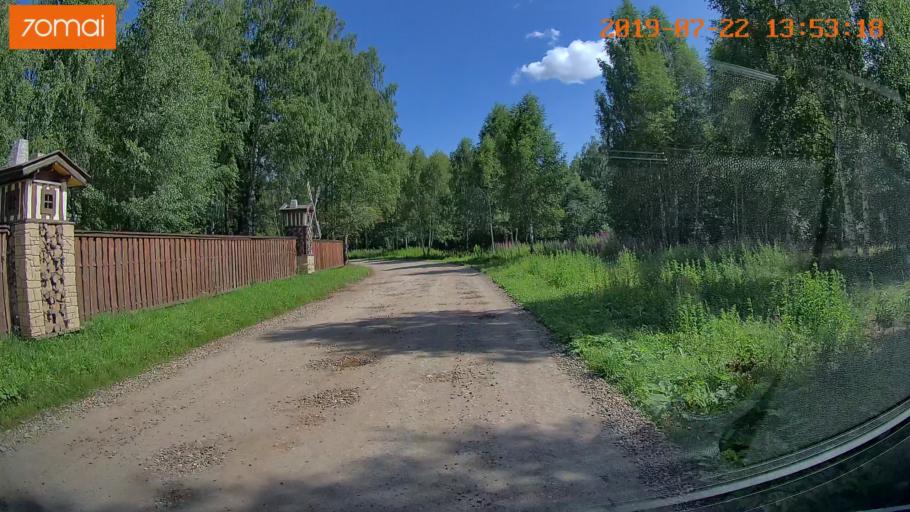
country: RU
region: Ivanovo
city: Novo-Talitsy
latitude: 57.0807
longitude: 40.8760
